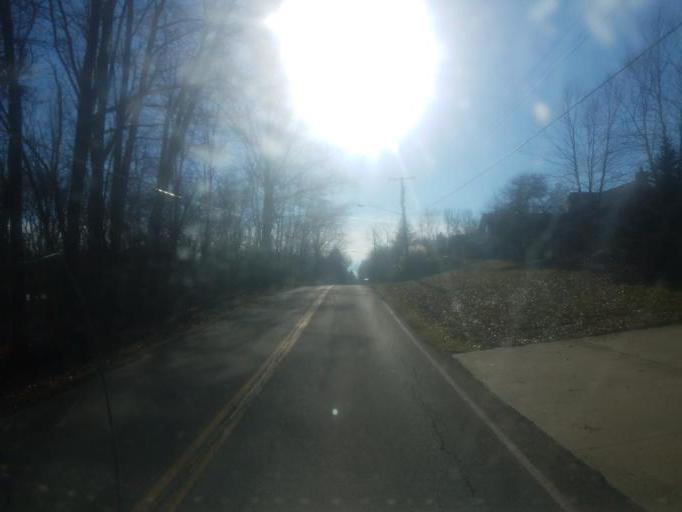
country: US
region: Ohio
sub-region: Richland County
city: Ontario
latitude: 40.7553
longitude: -82.6340
